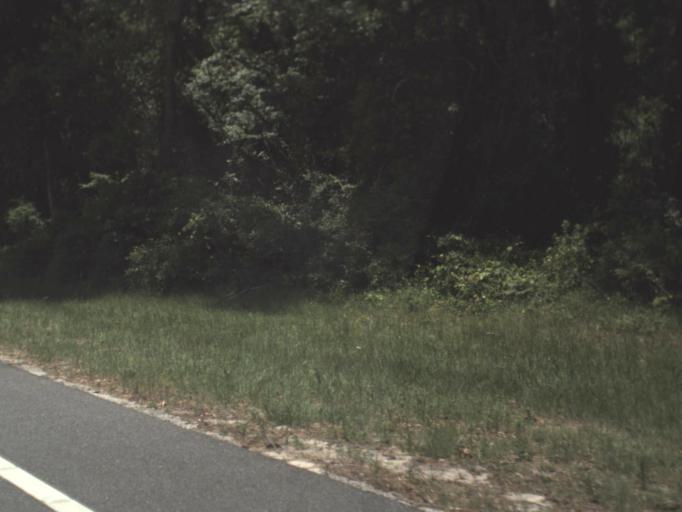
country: US
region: Florida
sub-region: Lafayette County
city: Mayo
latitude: 29.9332
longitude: -82.9494
